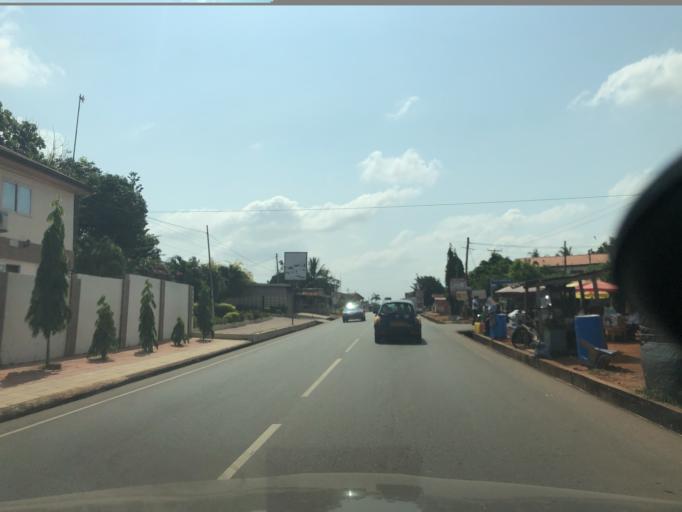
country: GH
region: Greater Accra
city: Medina Estates
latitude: 5.6729
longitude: -0.1903
